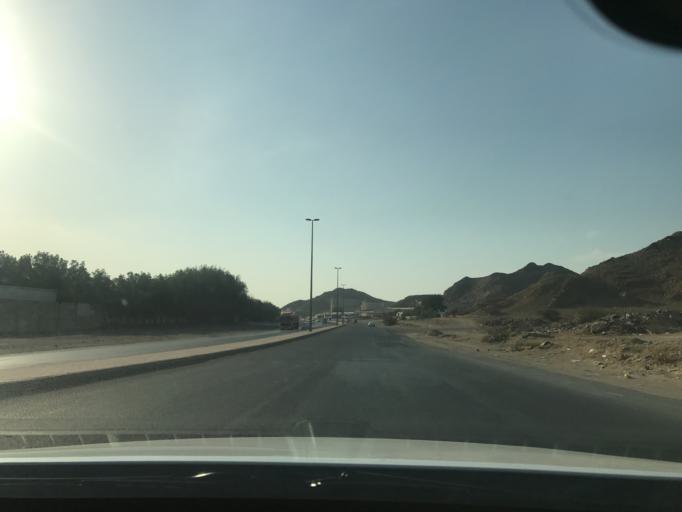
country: SA
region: Makkah
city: Jeddah
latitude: 21.4067
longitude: 39.4275
